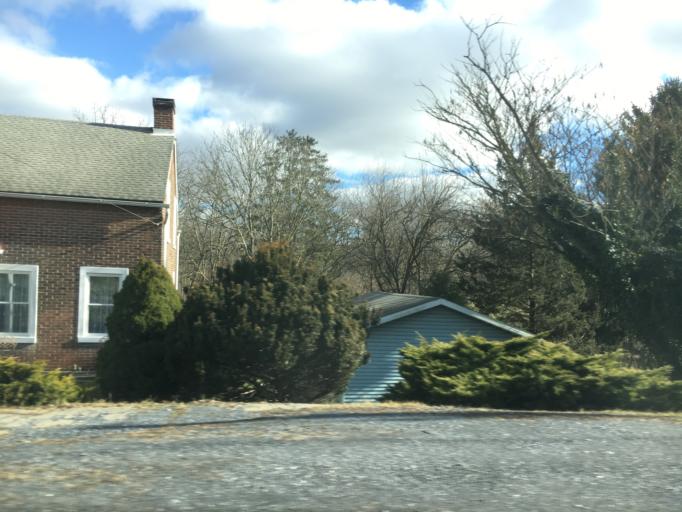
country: US
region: Pennsylvania
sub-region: Lehigh County
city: Egypt
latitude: 40.6744
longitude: -75.5257
